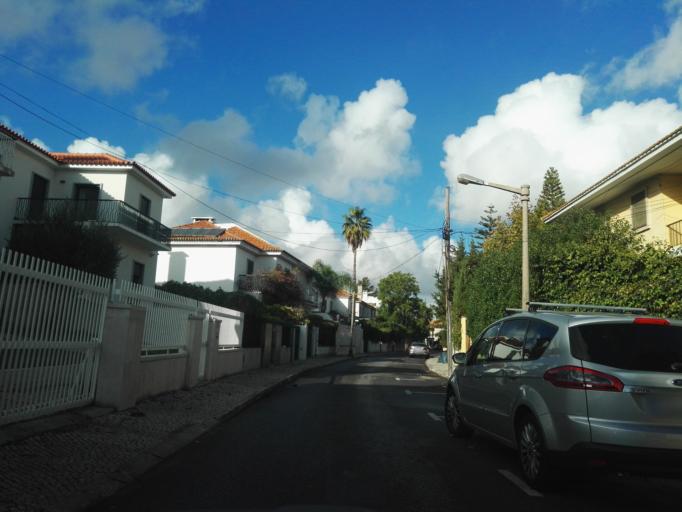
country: PT
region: Lisbon
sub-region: Lisbon
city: Lisbon
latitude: 38.7518
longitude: -9.1321
